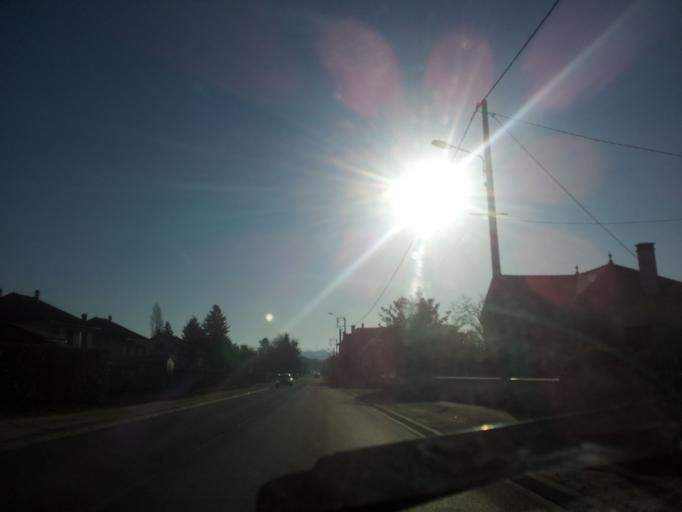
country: FR
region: Auvergne
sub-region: Departement de l'Allier
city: Saint-Pourcain-sur-Sioule
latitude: 46.3119
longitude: 3.2785
